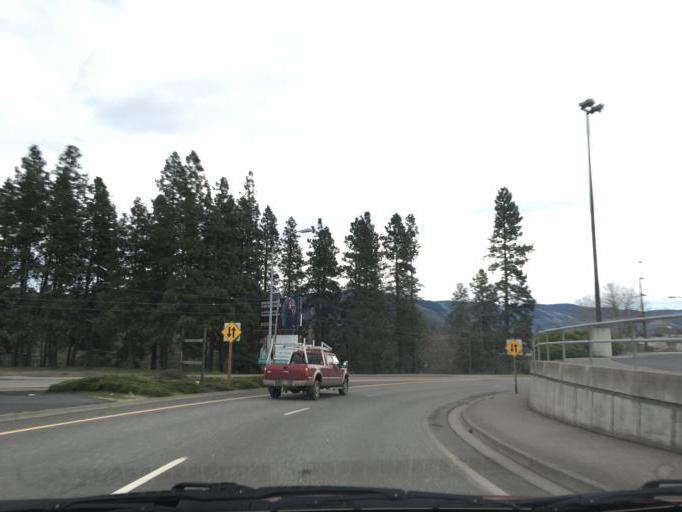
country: US
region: Oregon
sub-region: Hood River County
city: Hood River
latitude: 45.6993
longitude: -121.5241
